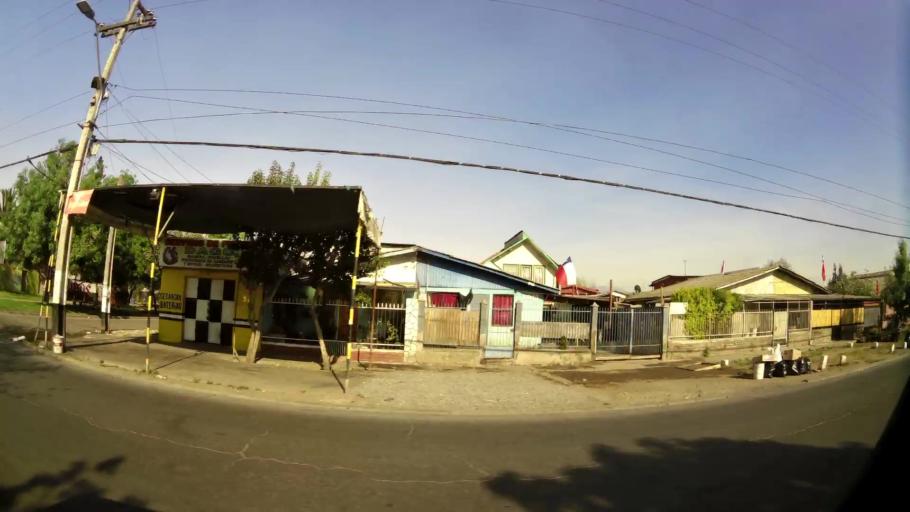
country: CL
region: Santiago Metropolitan
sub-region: Provincia de Santiago
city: Lo Prado
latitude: -33.4178
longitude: -70.7530
